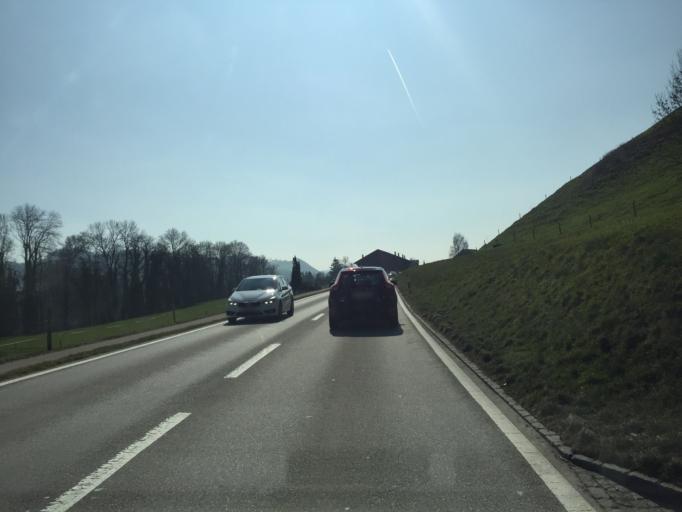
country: CH
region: Saint Gallen
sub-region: Wahlkreis Toggenburg
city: Lutisburg
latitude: 47.3907
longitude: 9.0759
